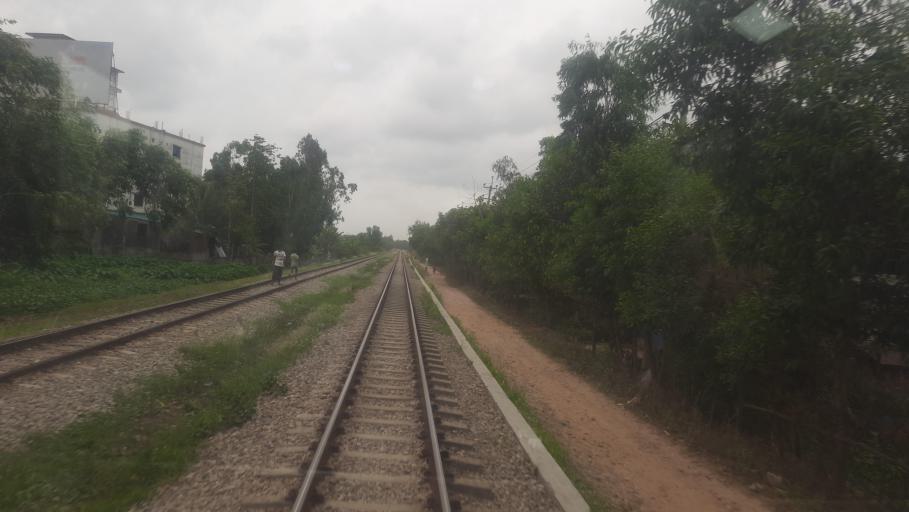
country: BD
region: Chittagong
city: Chhagalnaiya
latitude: 22.9002
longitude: 91.5341
